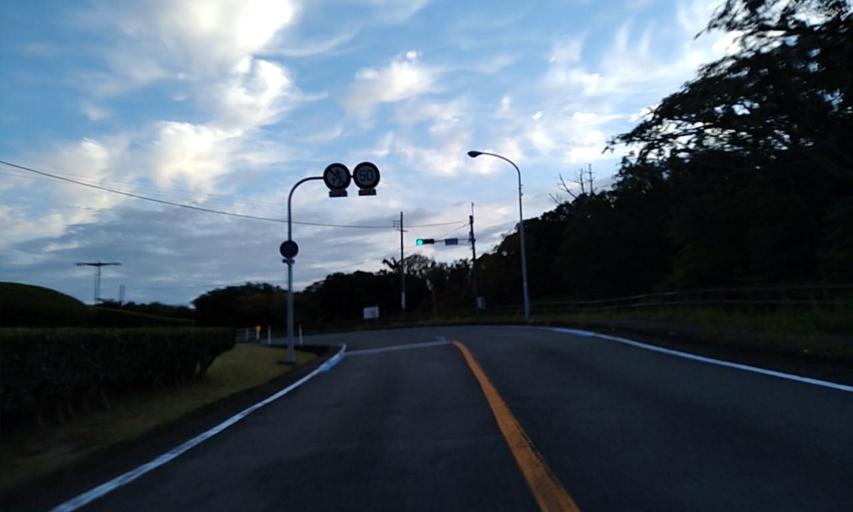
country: JP
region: Wakayama
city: Tanabe
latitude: 33.6632
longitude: 135.3410
